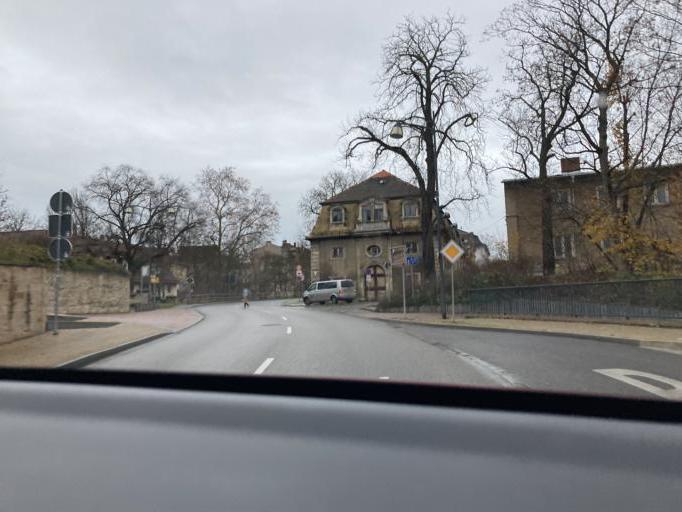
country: DE
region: Saxony-Anhalt
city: Weissenfels
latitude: 51.1997
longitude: 11.9768
